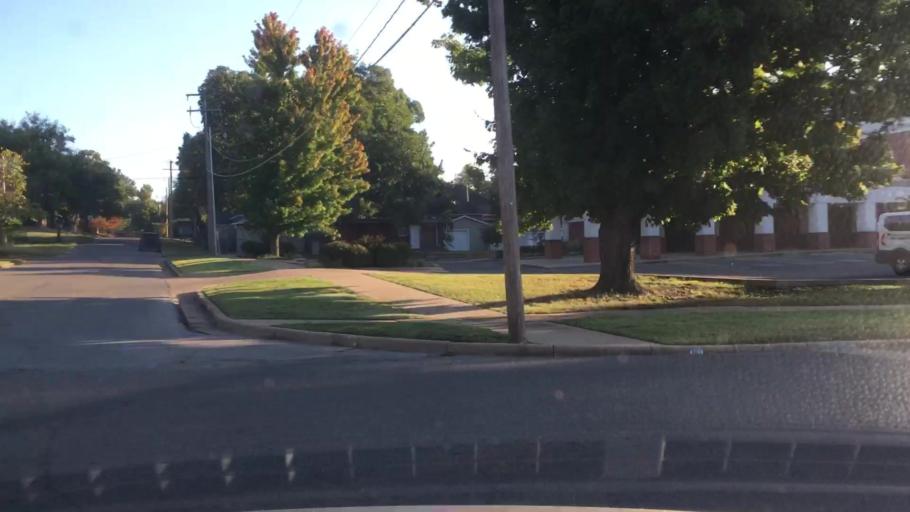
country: US
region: Oklahoma
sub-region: Cherokee County
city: Tahlequah
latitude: 35.9146
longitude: -94.9750
